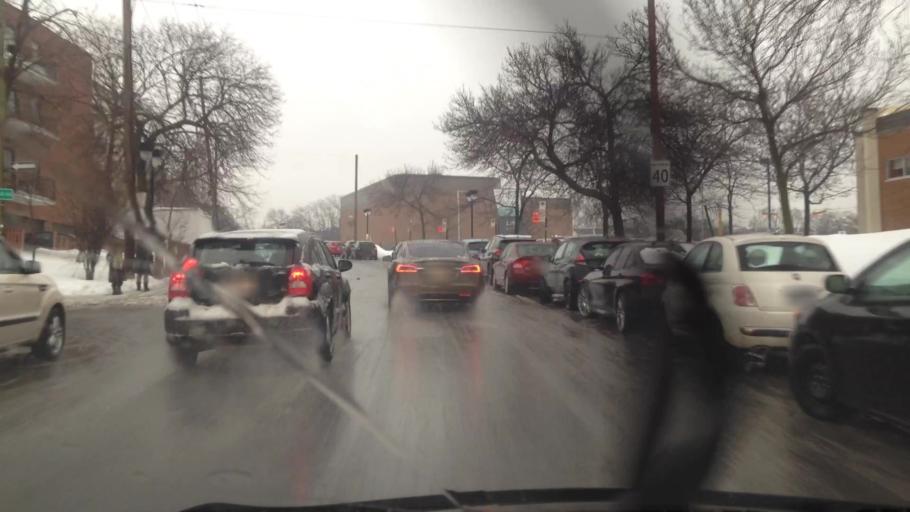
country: CA
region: Quebec
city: Mont-Royal
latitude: 45.5086
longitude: -73.6286
